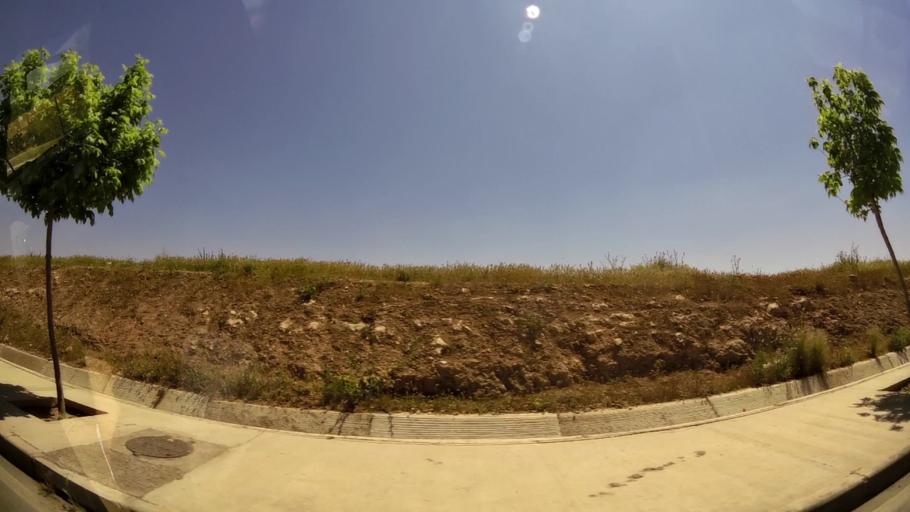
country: MA
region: Oriental
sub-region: Oujda-Angad
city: Oujda
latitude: 34.6948
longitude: -1.9288
